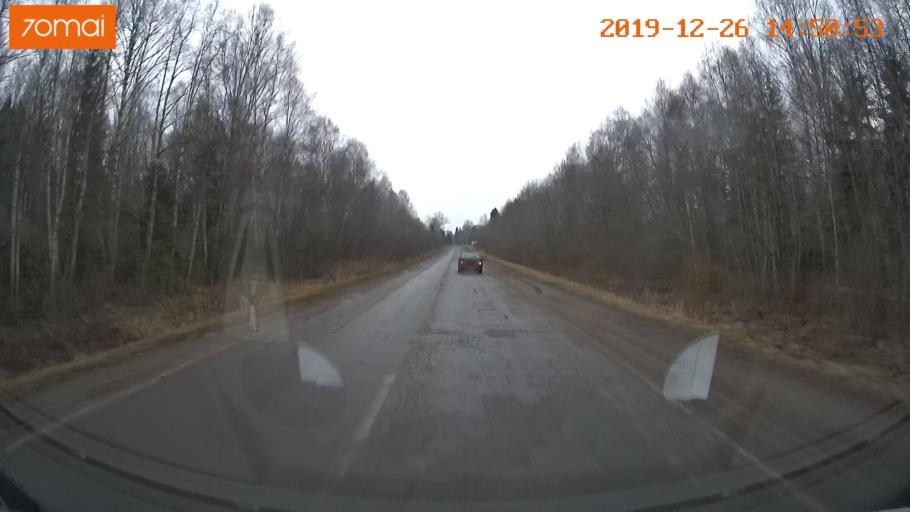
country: RU
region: Jaroslavl
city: Poshekhon'ye
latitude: 58.3287
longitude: 38.9185
